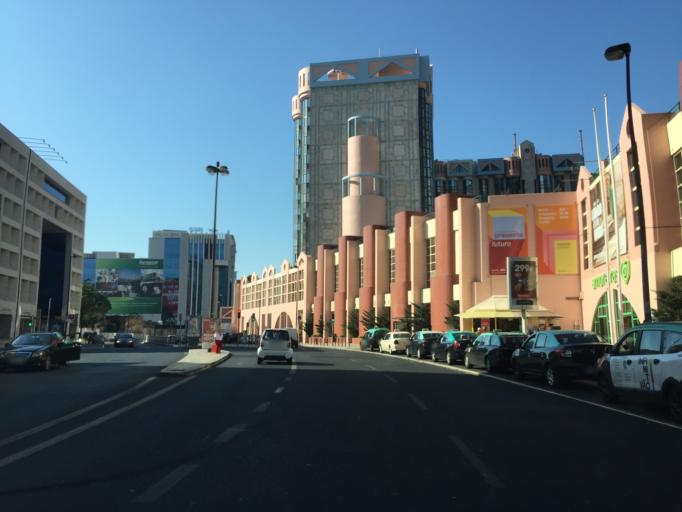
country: PT
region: Lisbon
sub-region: Lisbon
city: Lisbon
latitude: 38.7236
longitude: -9.1610
